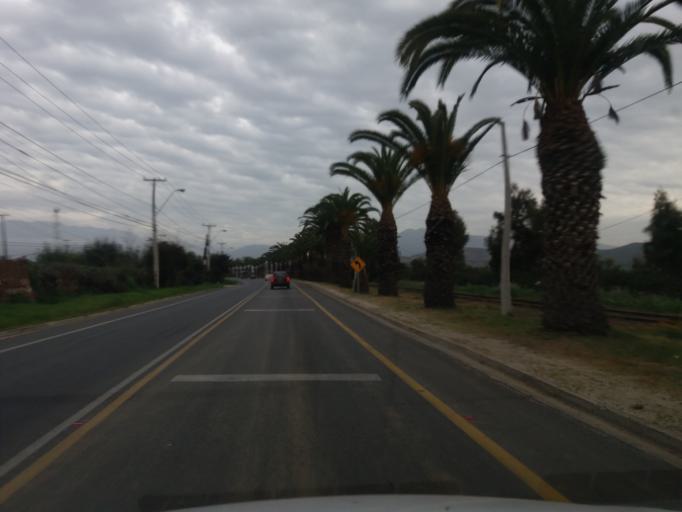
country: CL
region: Valparaiso
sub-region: Provincia de Marga Marga
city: Limache
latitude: -32.9769
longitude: -71.2811
